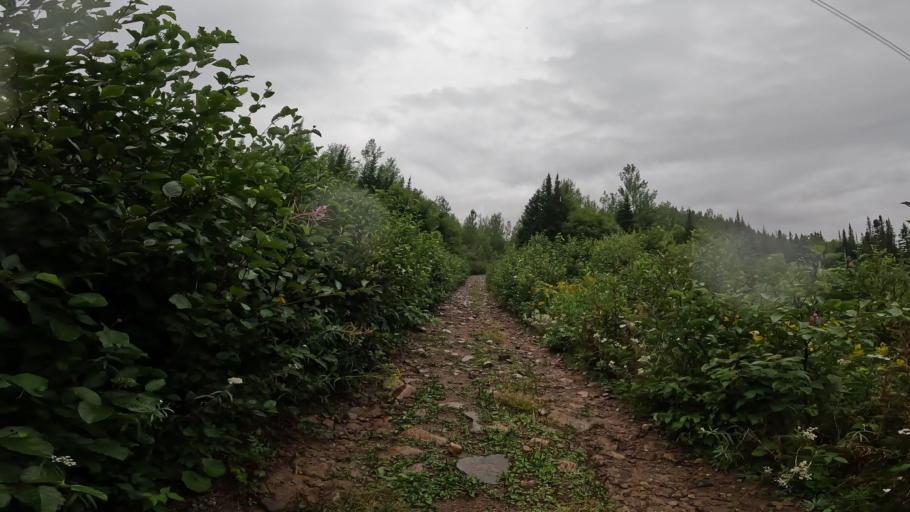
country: CA
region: Quebec
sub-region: Capitale-Nationale
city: La Malbaie
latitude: 47.8122
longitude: -70.4843
